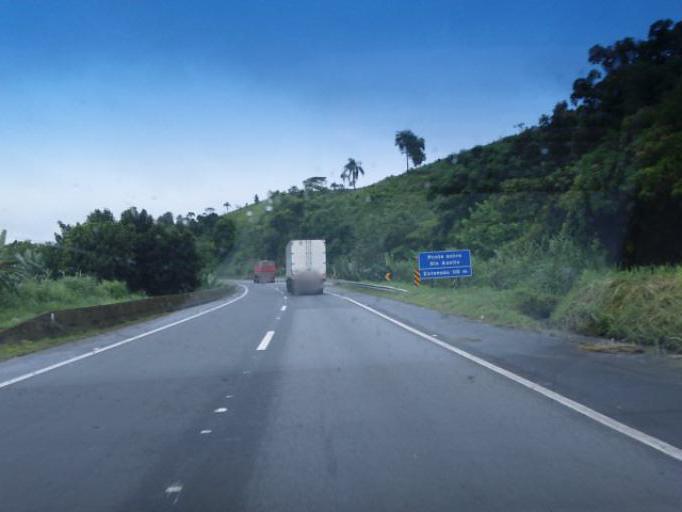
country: BR
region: Sao Paulo
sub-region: Cajati
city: Cajati
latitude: -24.7840
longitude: -48.1735
